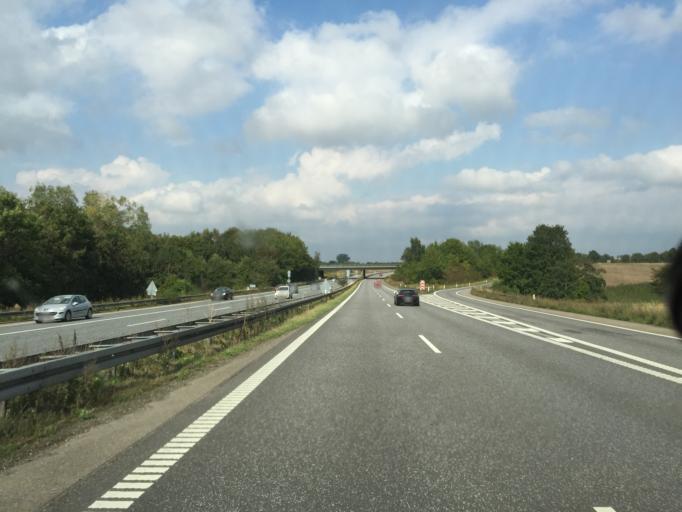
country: DK
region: Zealand
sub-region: Slagelse Kommune
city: Slagelse
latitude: 55.4155
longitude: 11.4124
